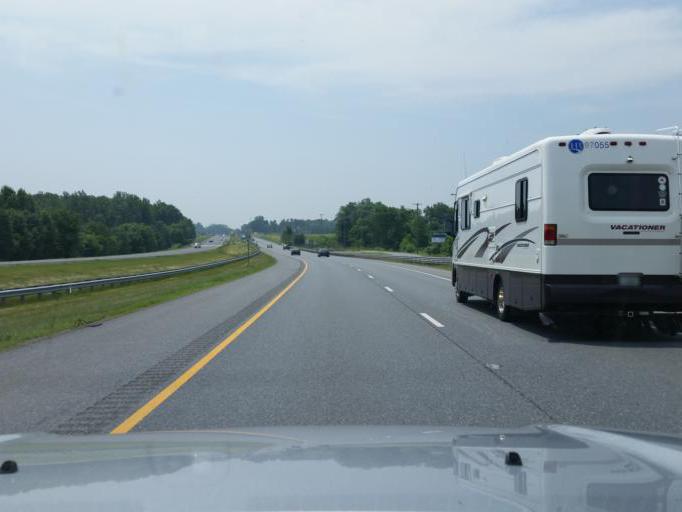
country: US
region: Maryland
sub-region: Frederick County
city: Clover Hill
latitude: 39.4668
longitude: -77.4022
